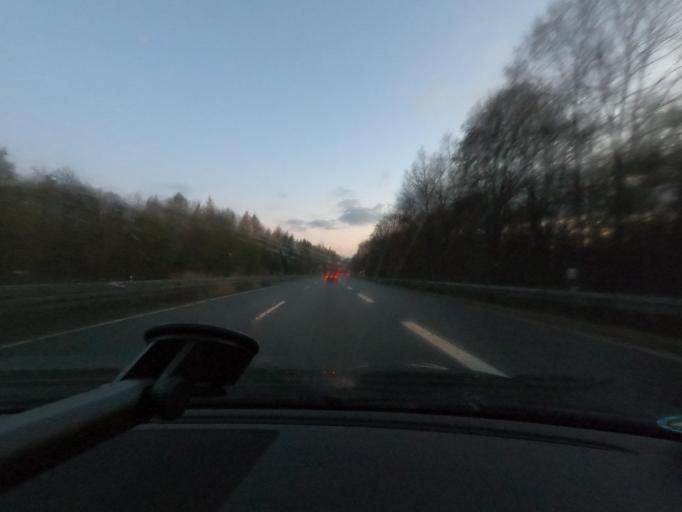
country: DE
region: Lower Saxony
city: Hoerden
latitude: 51.6870
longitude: 10.3031
